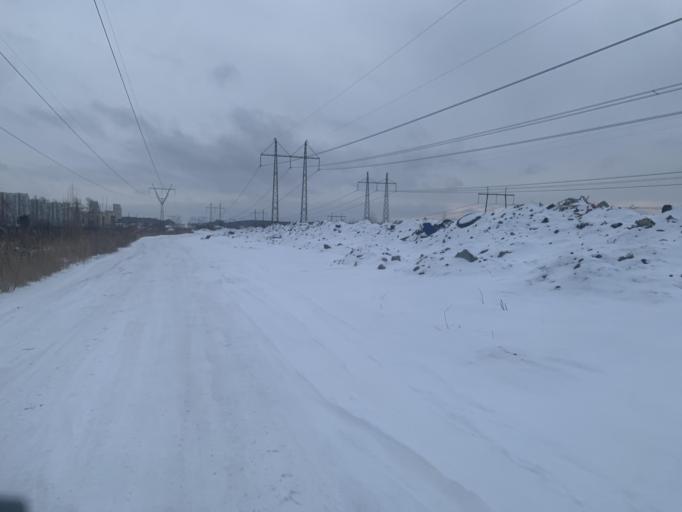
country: RU
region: Chelyabinsk
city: Roshchino
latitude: 55.1871
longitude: 61.2579
